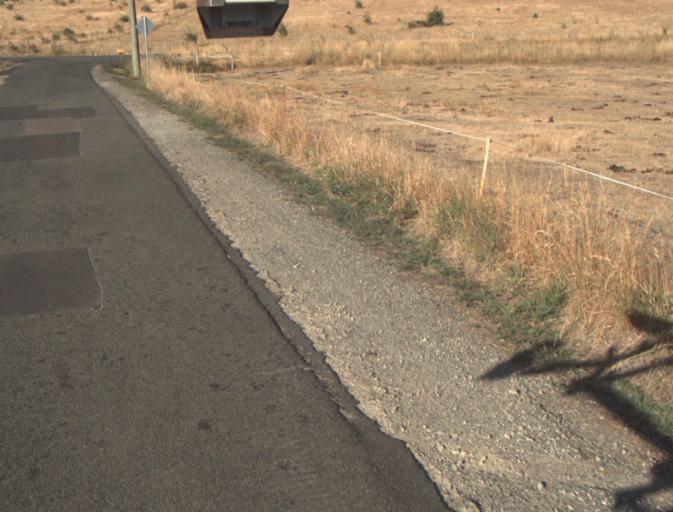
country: AU
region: Tasmania
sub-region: Launceston
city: Newstead
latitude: -41.4376
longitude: 147.2103
